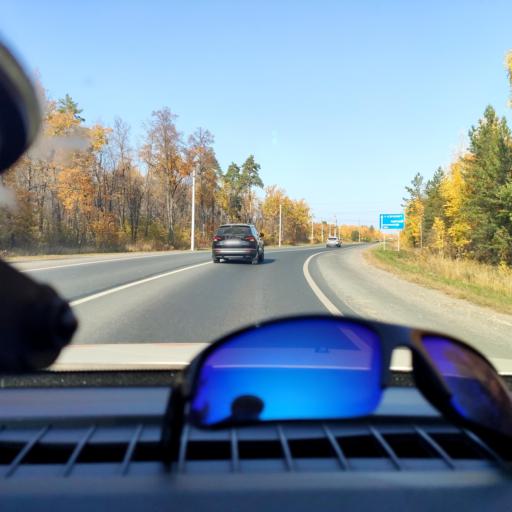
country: RU
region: Samara
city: Volzhskiy
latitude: 53.4475
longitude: 50.1227
